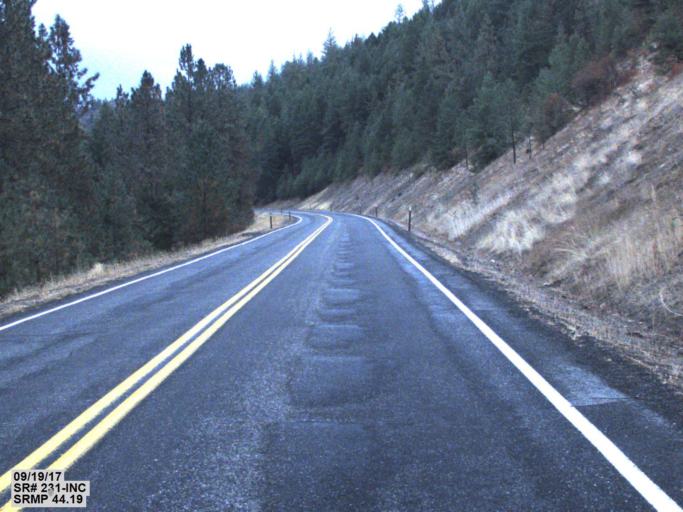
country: US
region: Washington
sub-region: Spokane County
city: Fairchild Air Force Base
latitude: 47.8383
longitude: -117.8607
